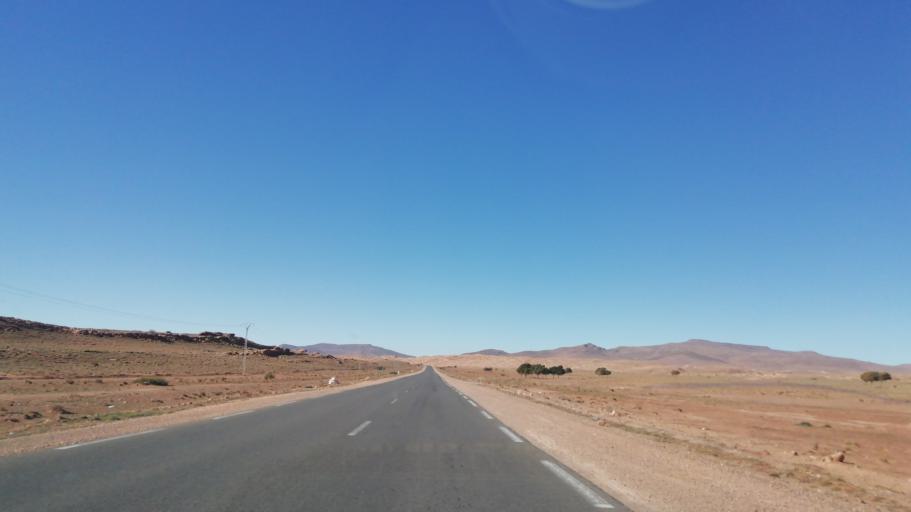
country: DZ
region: El Bayadh
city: El Bayadh
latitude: 33.6156
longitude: 1.2117
